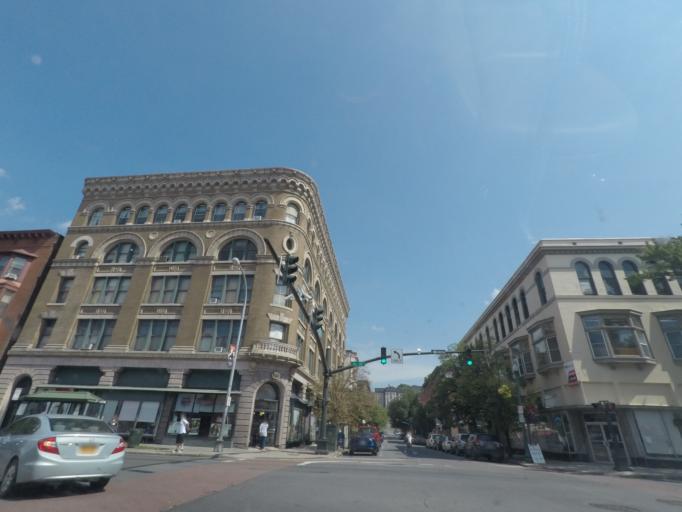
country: US
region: New York
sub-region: Rensselaer County
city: Troy
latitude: 42.7324
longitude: -73.6890
